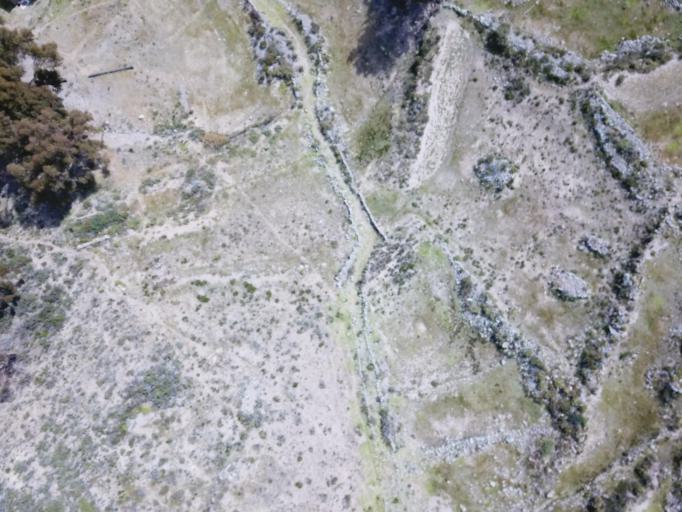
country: BO
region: La Paz
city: Achacachi
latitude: -16.0548
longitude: -68.8098
